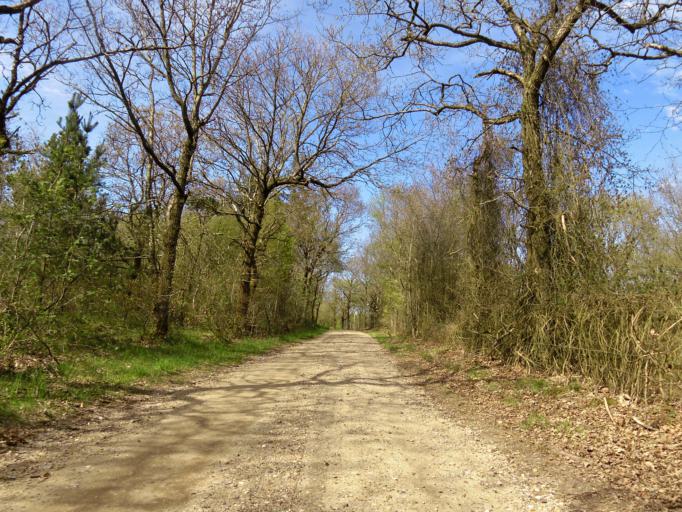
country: DK
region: Central Jutland
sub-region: Holstebro Kommune
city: Vinderup
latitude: 56.4823
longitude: 8.8712
